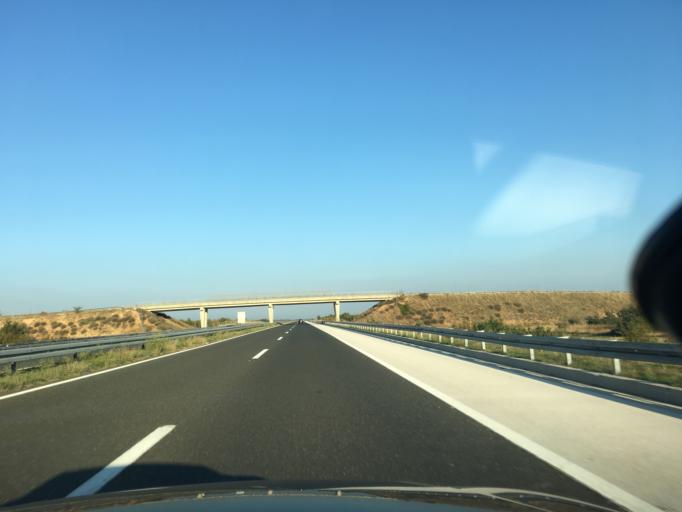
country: HR
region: Zadarska
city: Benkovac
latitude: 43.9551
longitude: 15.6770
